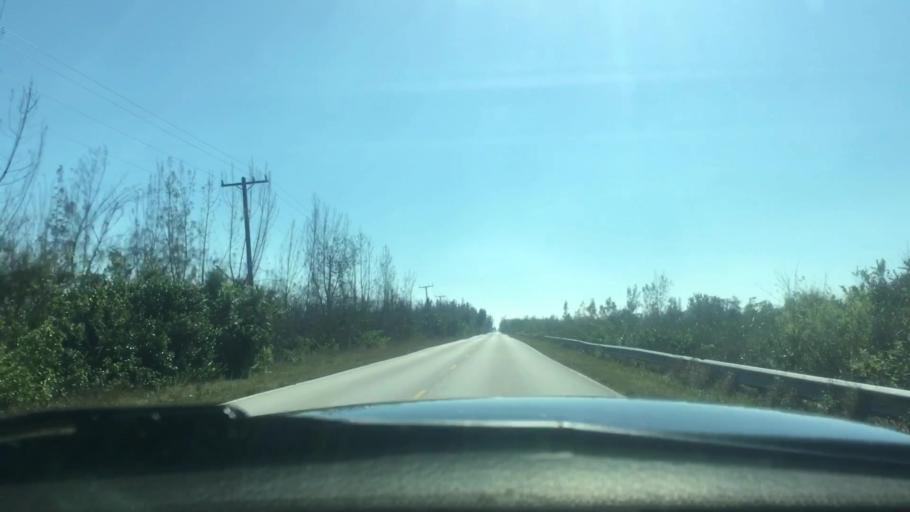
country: US
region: Florida
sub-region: Miami-Dade County
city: Florida City
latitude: 25.4259
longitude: -80.4683
